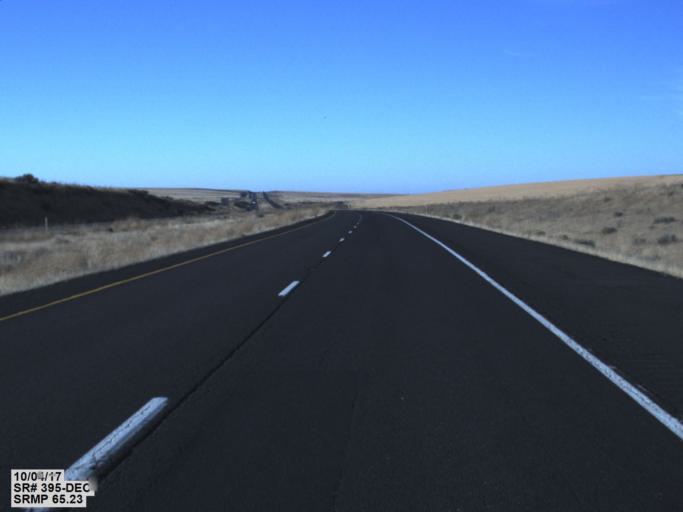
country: US
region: Washington
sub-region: Franklin County
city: Connell
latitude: 46.7806
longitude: -118.7672
